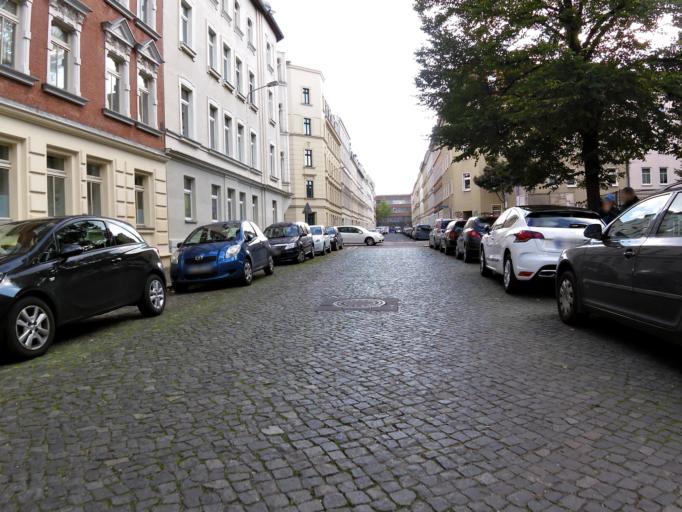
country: DE
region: Saxony
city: Leipzig
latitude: 51.3323
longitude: 12.3299
